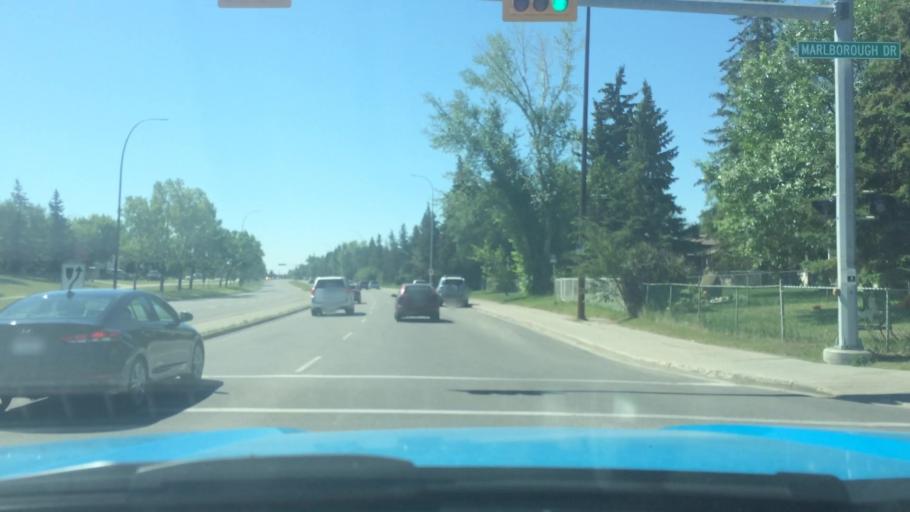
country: CA
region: Alberta
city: Calgary
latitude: 51.0600
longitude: -113.9585
